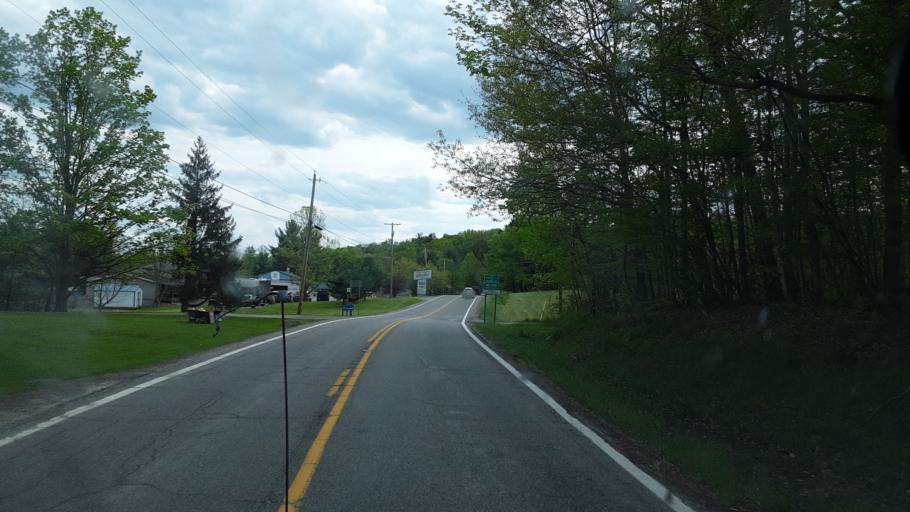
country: US
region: Ohio
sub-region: Portage County
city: Garrettsville
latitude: 41.3484
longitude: -81.0395
